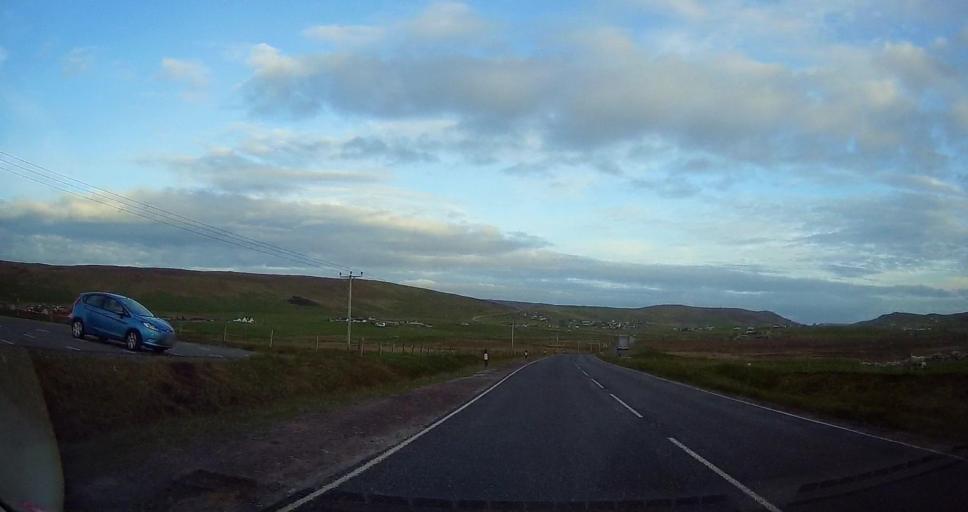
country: GB
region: Scotland
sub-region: Shetland Islands
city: Lerwick
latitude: 60.1984
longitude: -1.2322
